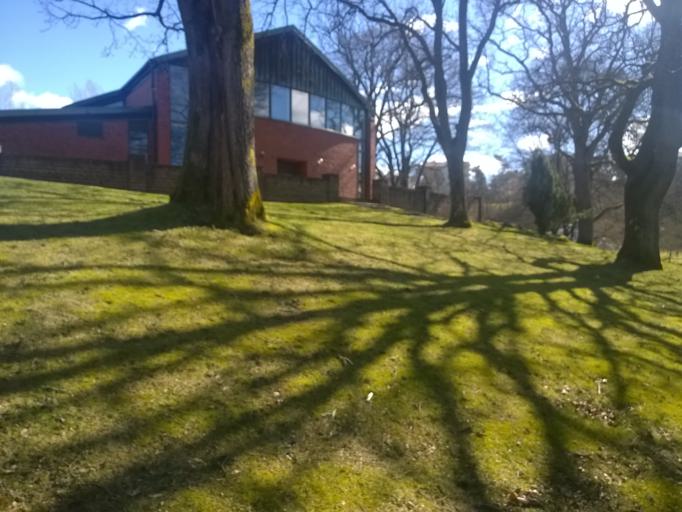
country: SE
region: Vaestra Goetaland
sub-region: Boras Kommun
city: Boras
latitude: 57.7247
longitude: 12.9081
